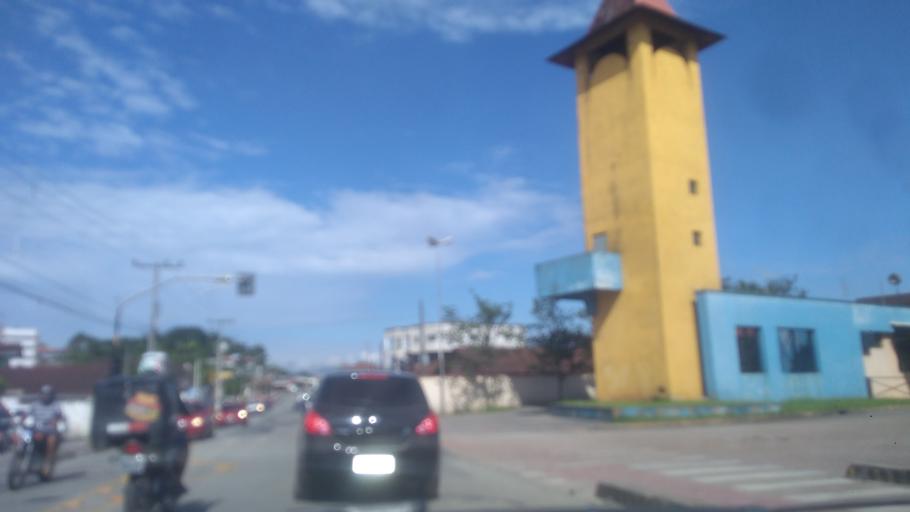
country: BR
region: Santa Catarina
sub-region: Joinville
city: Joinville
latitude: -26.3200
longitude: -48.8223
